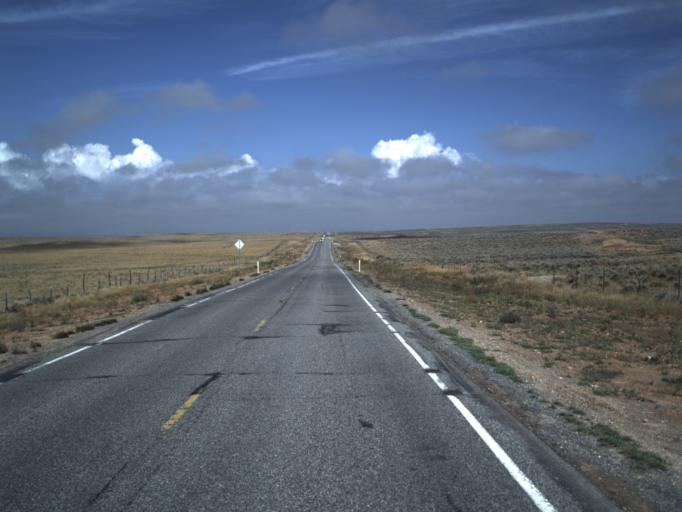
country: US
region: Wyoming
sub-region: Uinta County
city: Evanston
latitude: 41.4266
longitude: -111.0552
